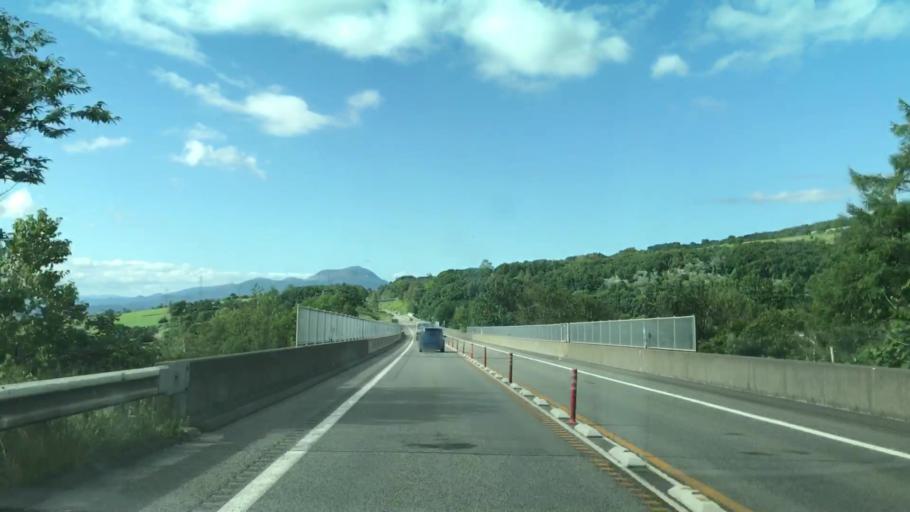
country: JP
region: Hokkaido
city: Date
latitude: 42.4314
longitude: 140.9246
